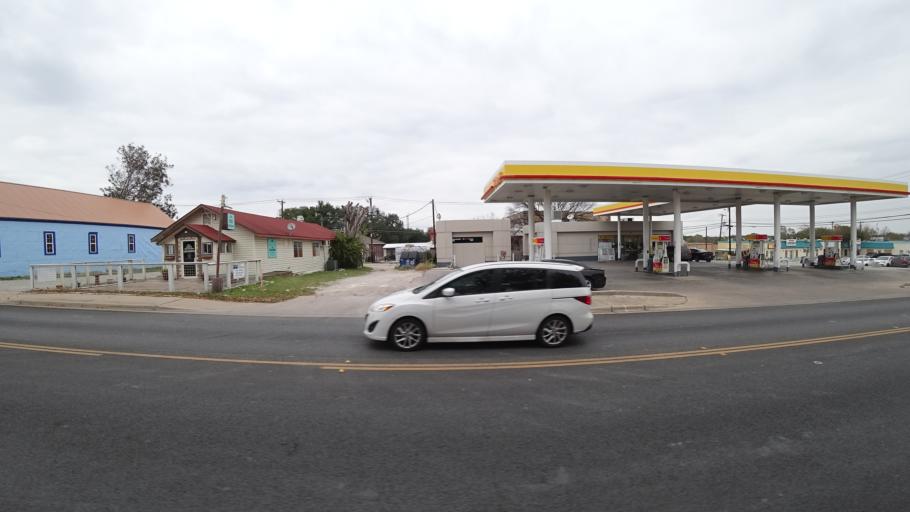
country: US
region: Texas
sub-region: Travis County
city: Pflugerville
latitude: 30.4396
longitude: -97.6204
